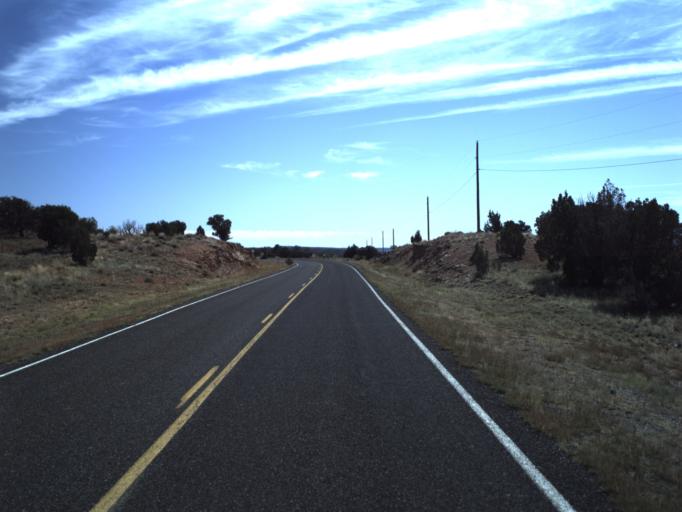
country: US
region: Utah
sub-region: Wayne County
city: Loa
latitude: 37.7297
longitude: -111.5351
